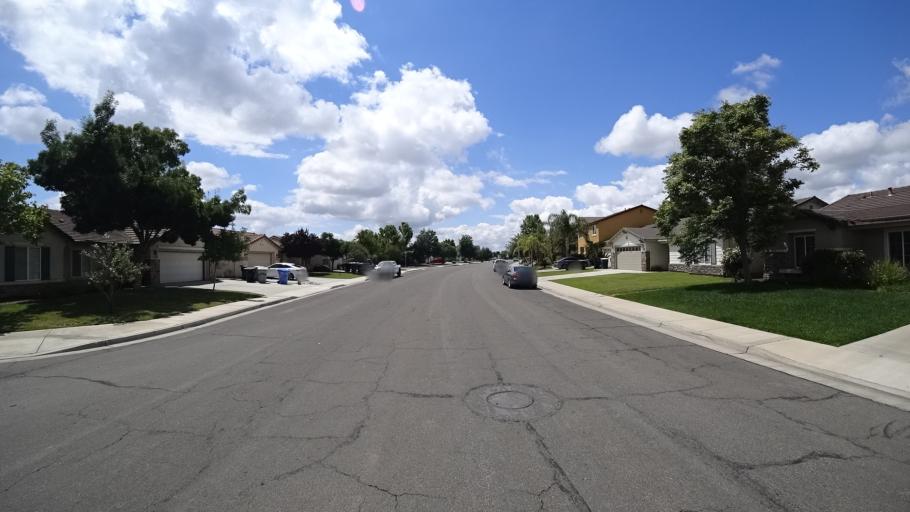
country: US
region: California
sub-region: Kings County
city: Lucerne
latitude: 36.3560
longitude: -119.6619
